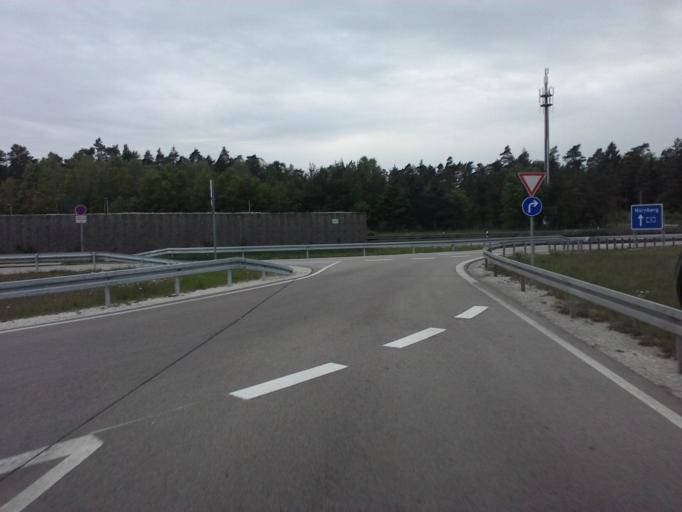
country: DE
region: Bavaria
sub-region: Regierungsbezirk Mittelfranken
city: Leinburg
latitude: 49.4370
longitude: 11.2706
